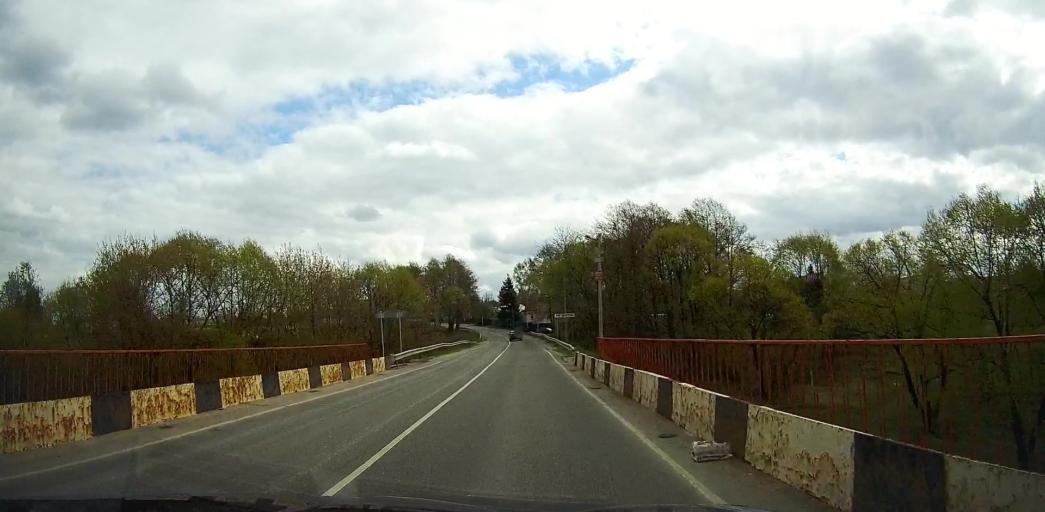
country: RU
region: Moskovskaya
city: Imeni Tsyurupy
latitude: 55.4962
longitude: 38.6307
